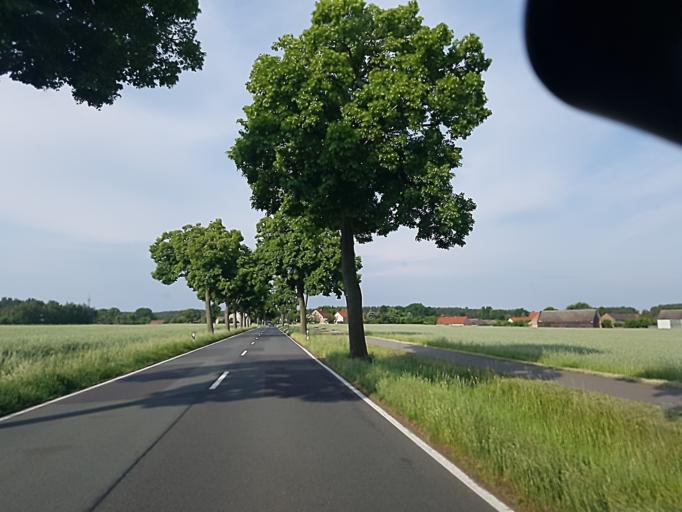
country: DE
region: Brandenburg
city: Niemegk
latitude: 52.0558
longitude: 12.6662
